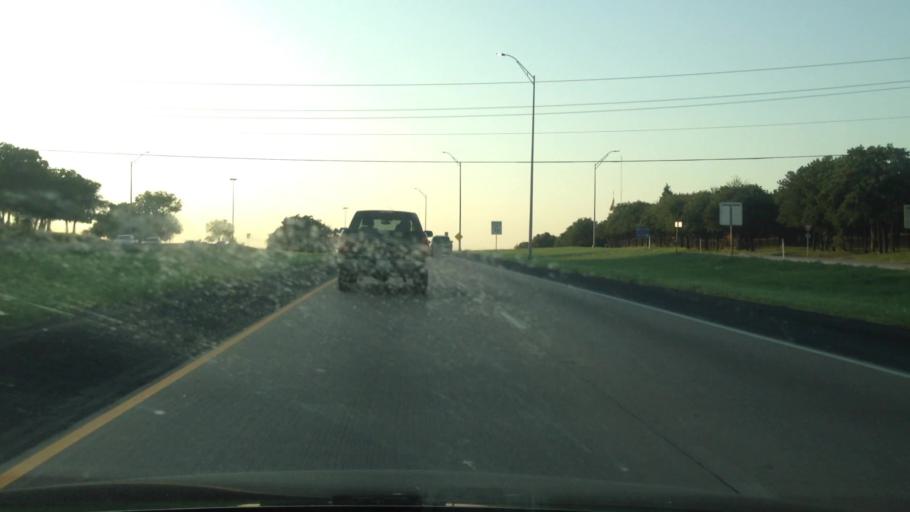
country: US
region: Texas
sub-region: Tarrant County
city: Kennedale
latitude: 32.6647
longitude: -97.2006
